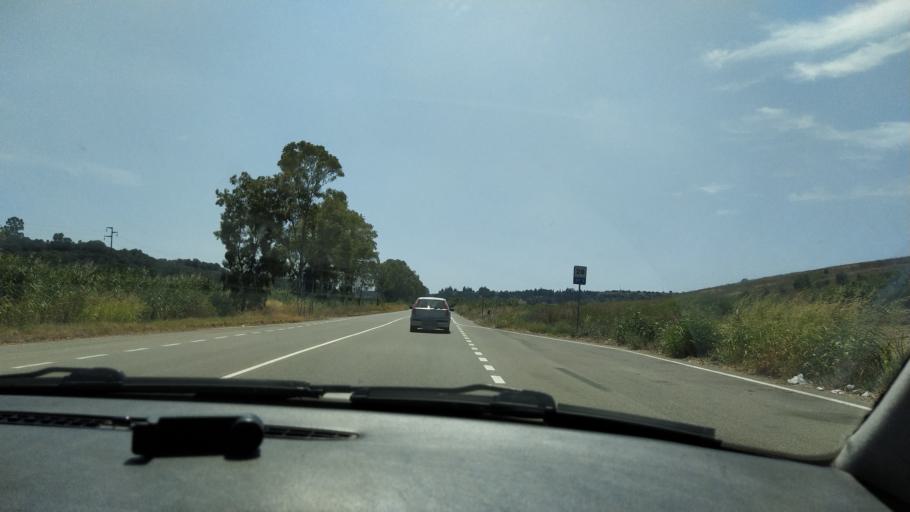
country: IT
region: Apulia
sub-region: Provincia di Taranto
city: Marina di Ginosa
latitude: 40.4402
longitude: 16.7839
